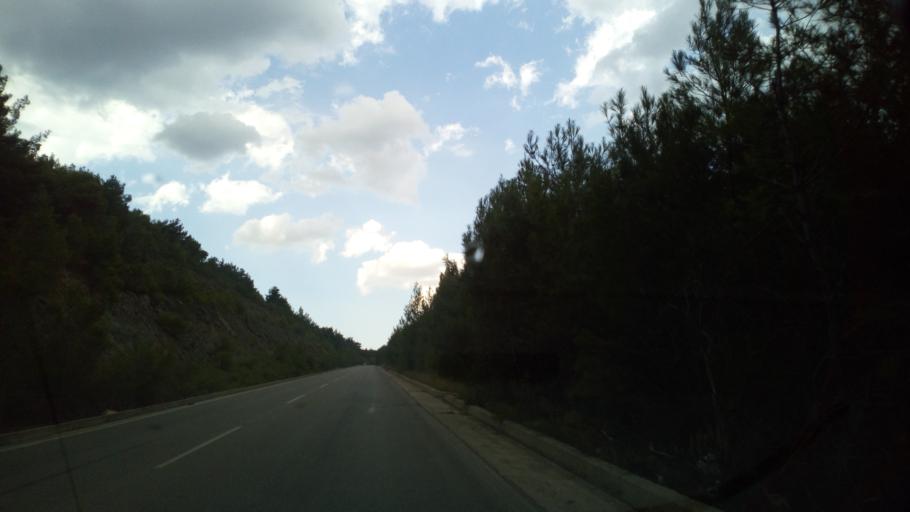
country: GR
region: Central Macedonia
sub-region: Nomos Chalkidikis
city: Polygyros
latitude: 40.3545
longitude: 23.4431
